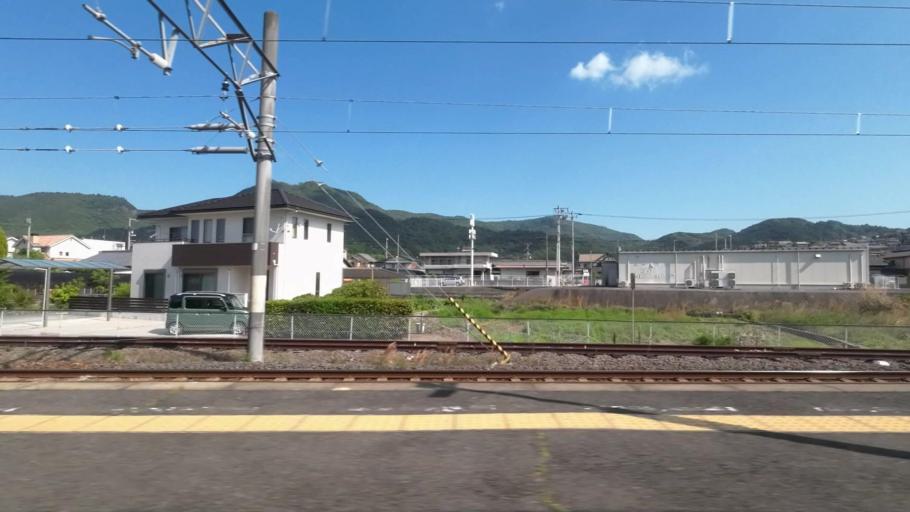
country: JP
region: Kagawa
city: Takamatsu-shi
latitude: 34.3054
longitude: 133.9692
